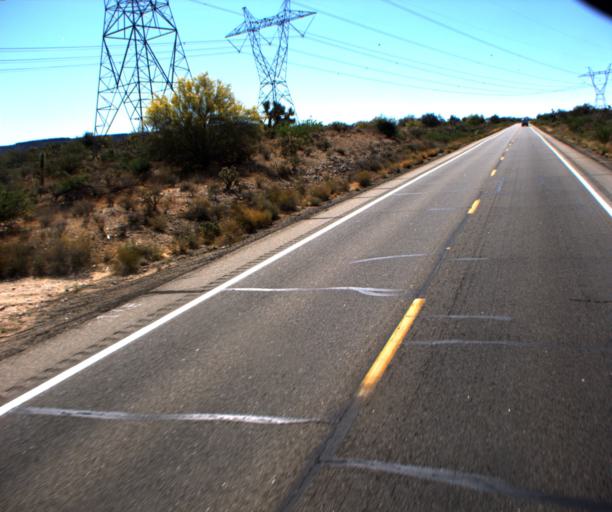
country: US
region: Arizona
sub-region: Yavapai County
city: Bagdad
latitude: 34.3404
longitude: -113.1532
